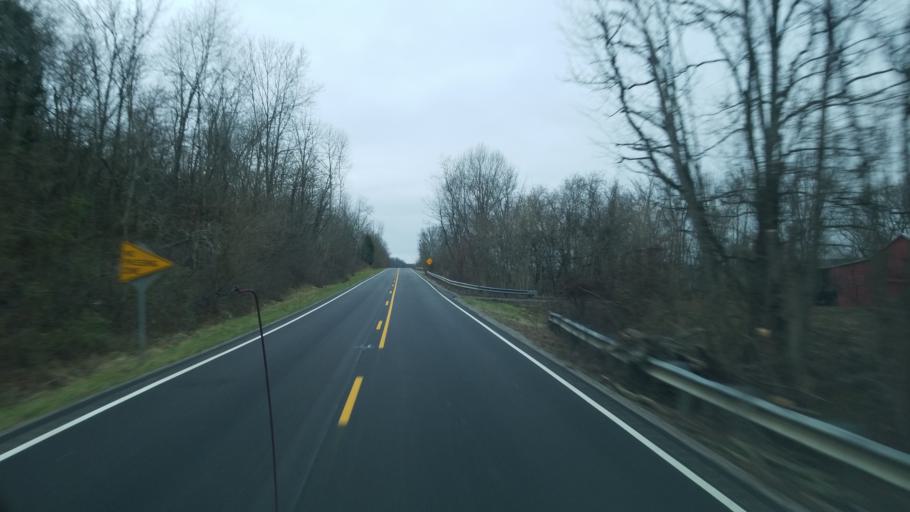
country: US
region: Kentucky
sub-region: Bracken County
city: Augusta
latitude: 38.7732
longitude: -83.9765
